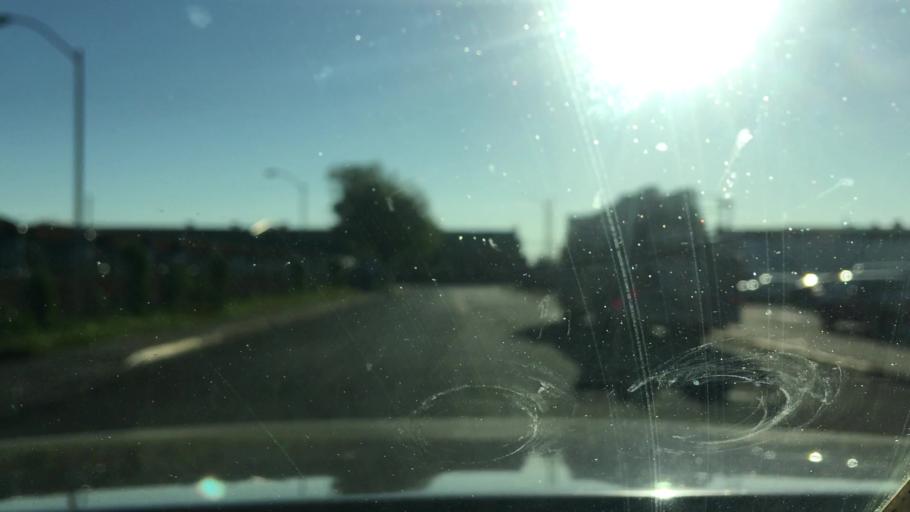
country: US
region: Oregon
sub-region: Lane County
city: Eugene
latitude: 44.0503
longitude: -123.1242
